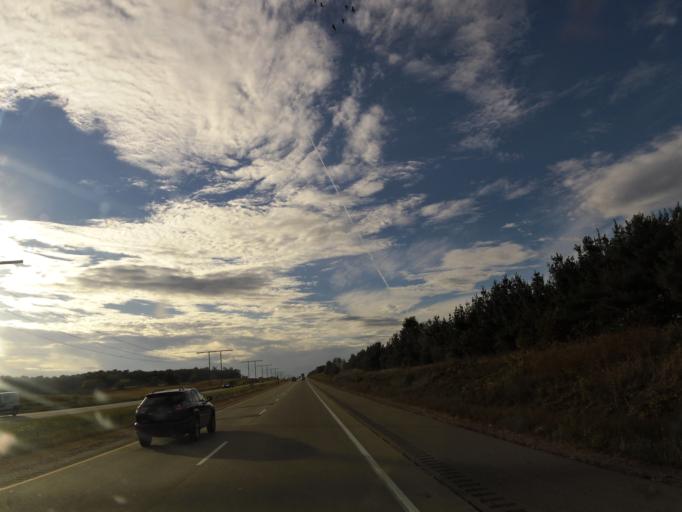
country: US
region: Wisconsin
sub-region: Sauk County
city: Baraboo
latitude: 43.5547
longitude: -89.6991
